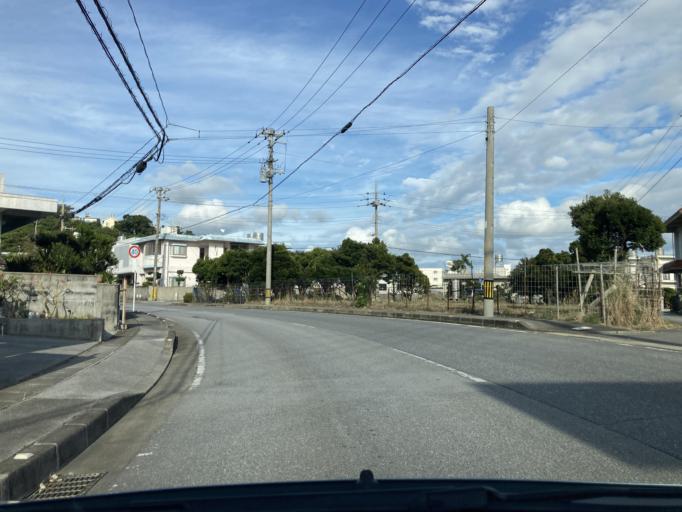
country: JP
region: Okinawa
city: Itoman
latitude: 26.1371
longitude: 127.7374
